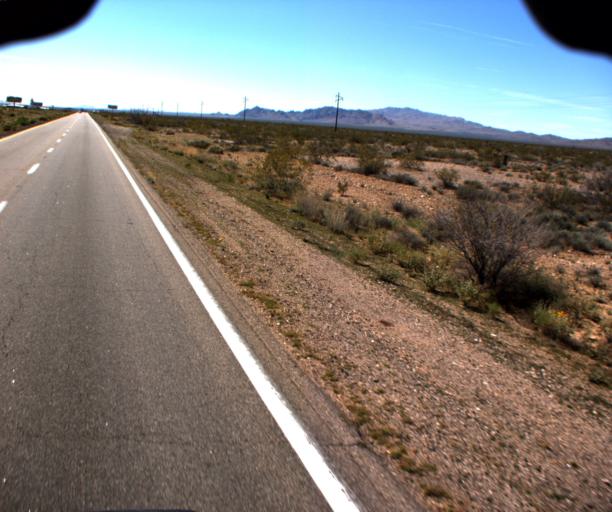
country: US
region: Arizona
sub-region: Mohave County
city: Dolan Springs
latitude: 35.7296
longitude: -114.4908
